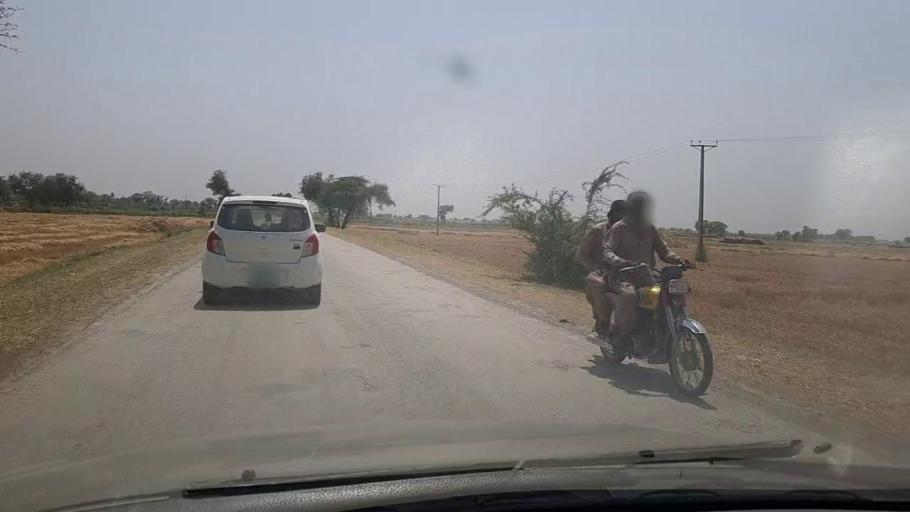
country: PK
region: Sindh
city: Miro Khan
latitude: 27.7197
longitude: 68.0684
